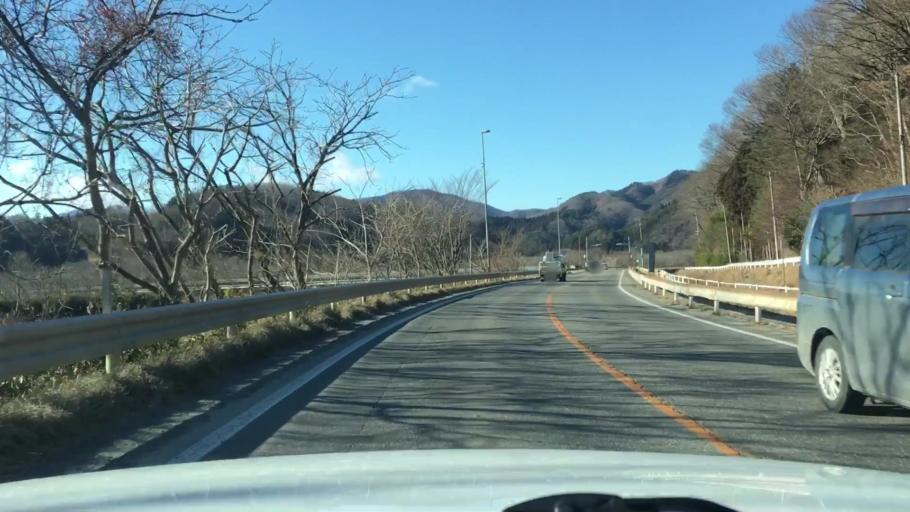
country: JP
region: Iwate
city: Miyako
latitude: 39.6290
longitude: 141.8575
